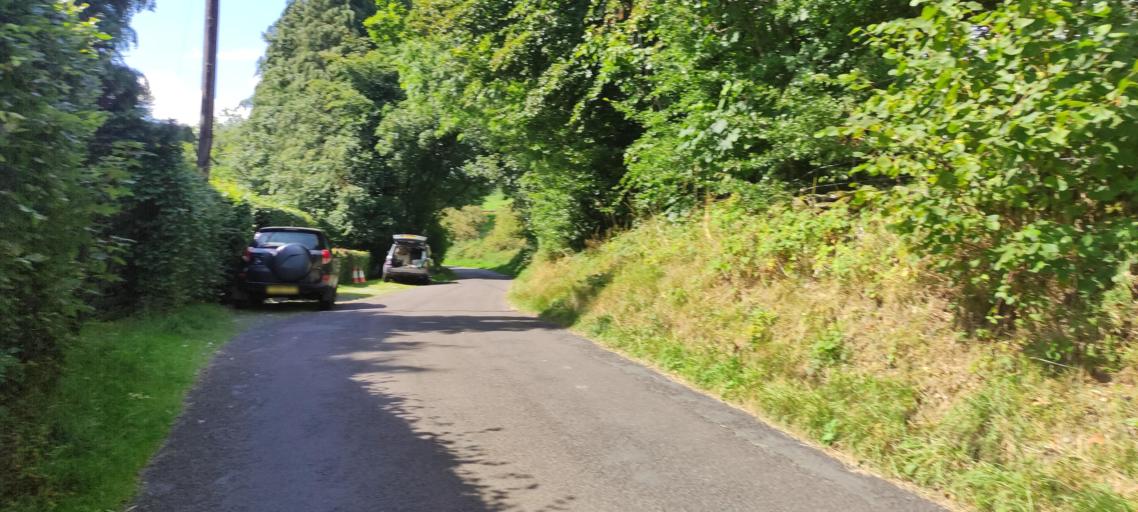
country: GB
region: England
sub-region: Cumbria
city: Penrith
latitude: 54.5391
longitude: -2.7584
